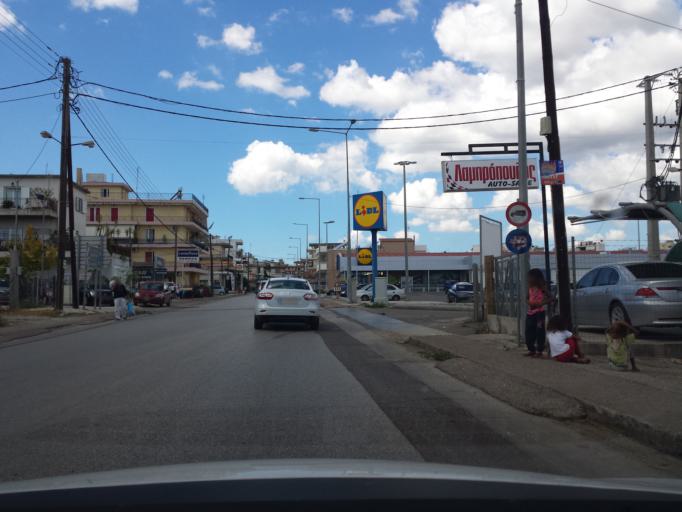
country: GR
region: West Greece
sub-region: Nomos Ileias
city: Pyrgos
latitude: 37.6685
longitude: 21.4506
